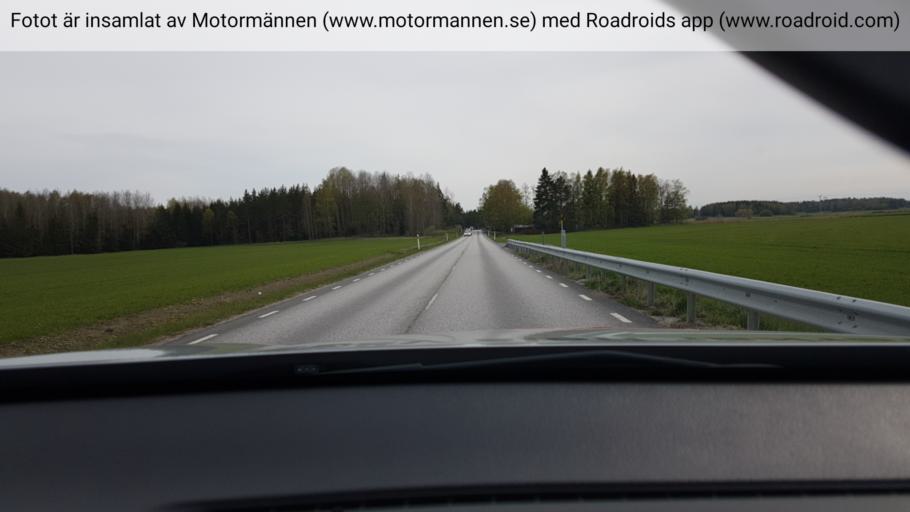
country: SE
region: Stockholm
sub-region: Sigtuna Kommun
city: Rosersberg
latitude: 59.5805
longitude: 17.9649
